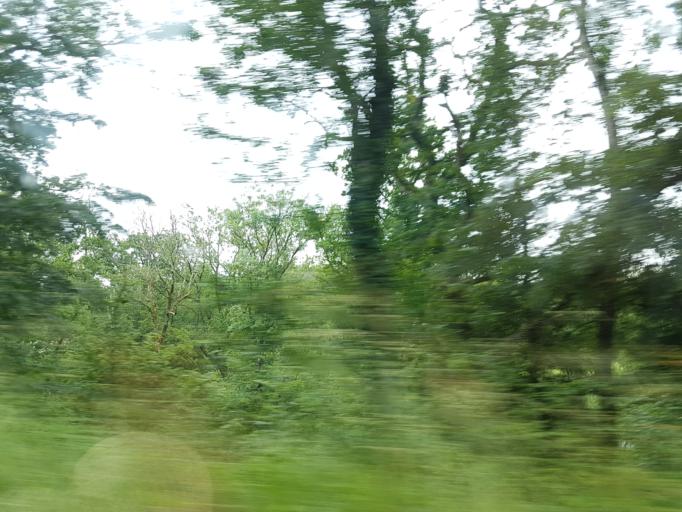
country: FR
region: Bourgogne
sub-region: Departement de la Nievre
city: Corbigny
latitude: 47.1926
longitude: 3.7283
